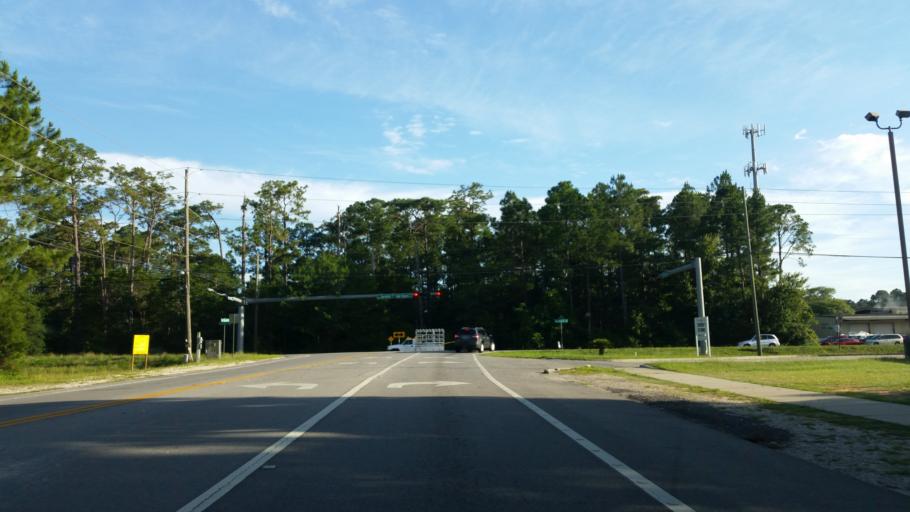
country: US
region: Florida
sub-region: Escambia County
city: Myrtle Grove
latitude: 30.3637
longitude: -87.3455
